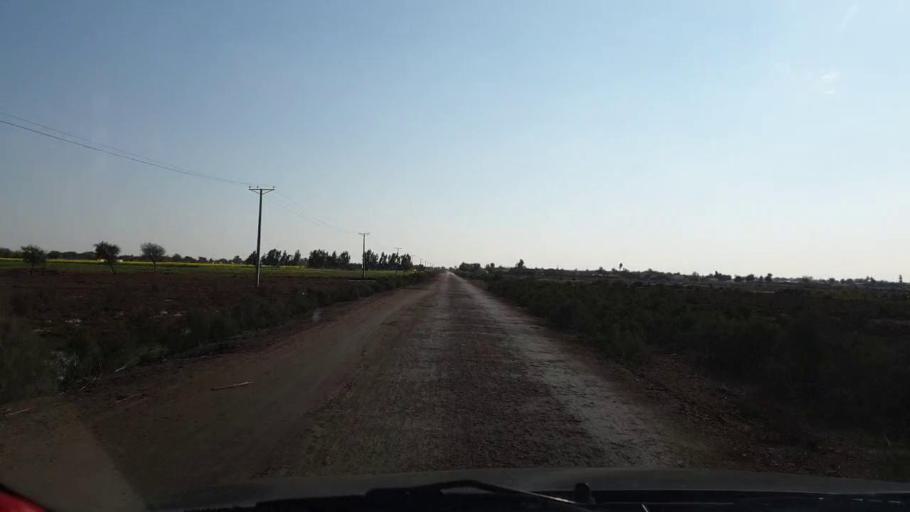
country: PK
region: Sindh
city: Sinjhoro
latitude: 25.9970
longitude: 68.8394
